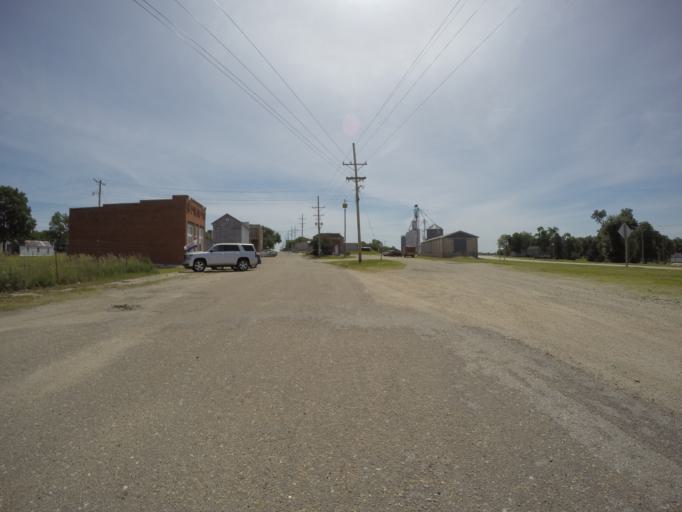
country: US
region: Kansas
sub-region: Washington County
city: Washington
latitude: 39.7118
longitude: -96.8740
